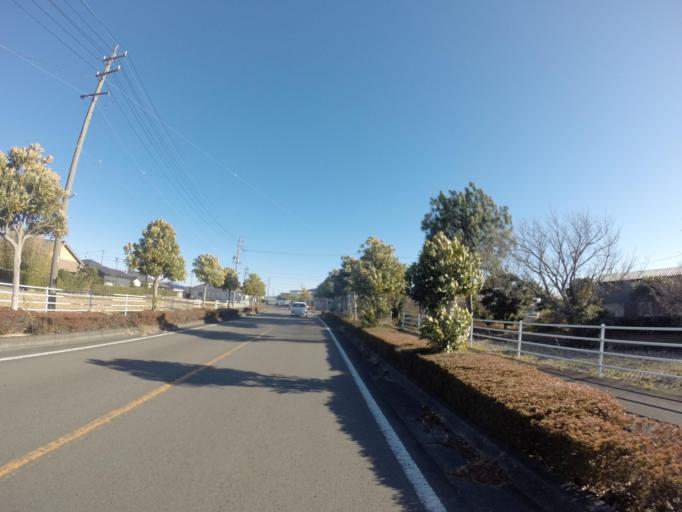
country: JP
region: Shizuoka
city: Fujieda
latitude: 34.8002
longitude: 138.2906
